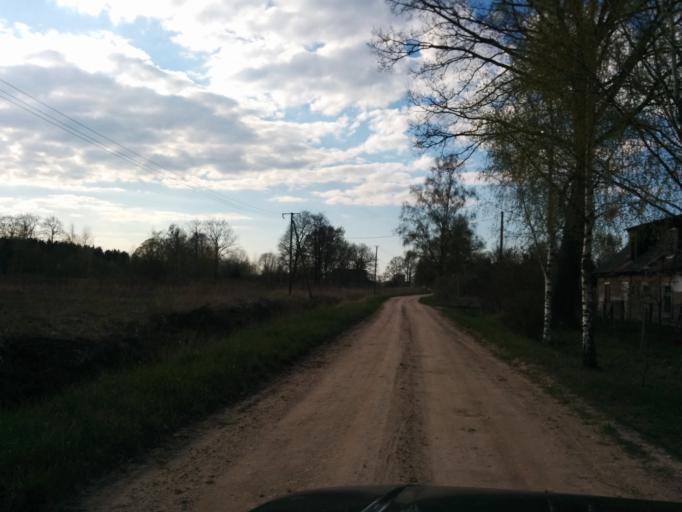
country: LV
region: Jelgava
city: Jelgava
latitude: 56.6772
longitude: 23.6671
